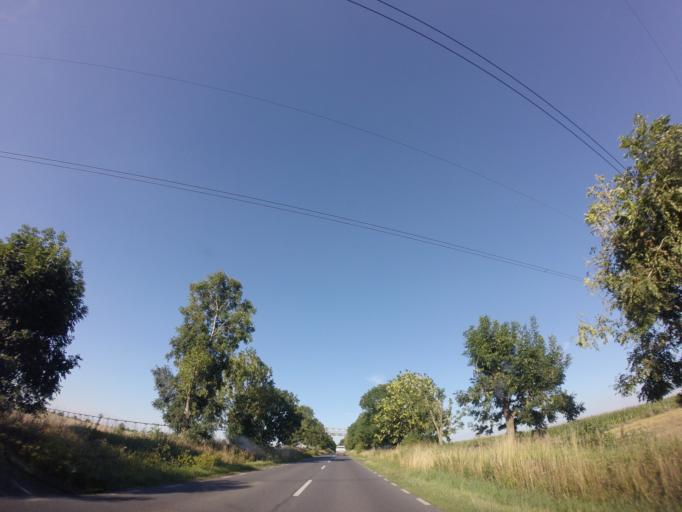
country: PL
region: Lubusz
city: Gorzow Wielkopolski
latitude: 52.7507
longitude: 15.3010
